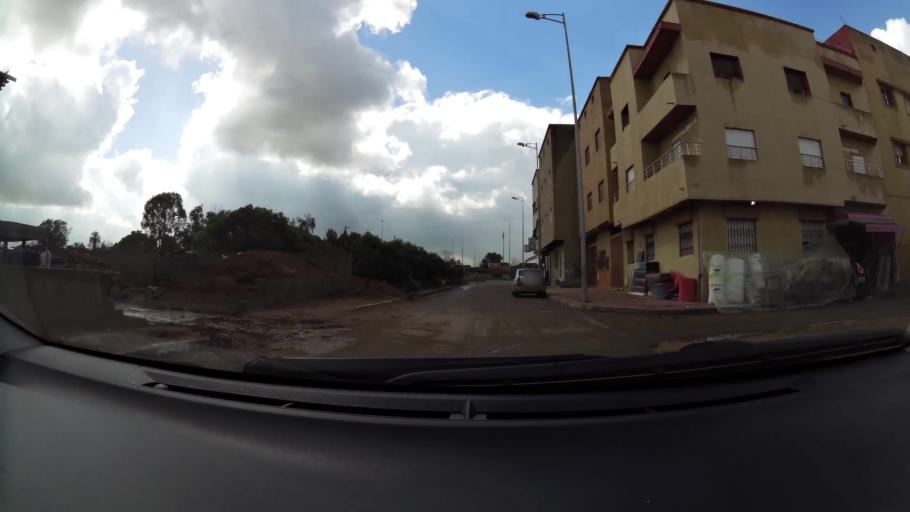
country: MA
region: Grand Casablanca
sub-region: Mediouna
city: Tit Mellil
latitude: 33.5501
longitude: -7.4818
